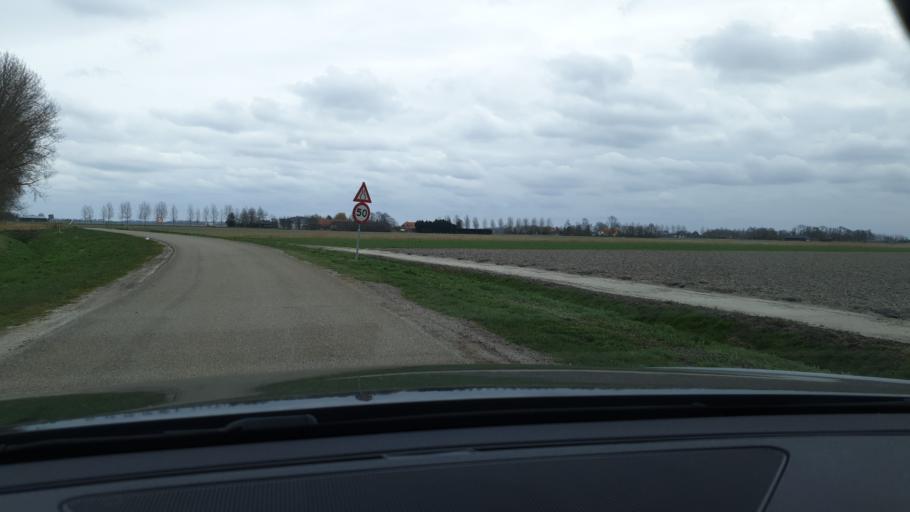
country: NL
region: Friesland
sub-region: Gemeente Lemsterland
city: Lemmer
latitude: 52.7828
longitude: 5.6814
